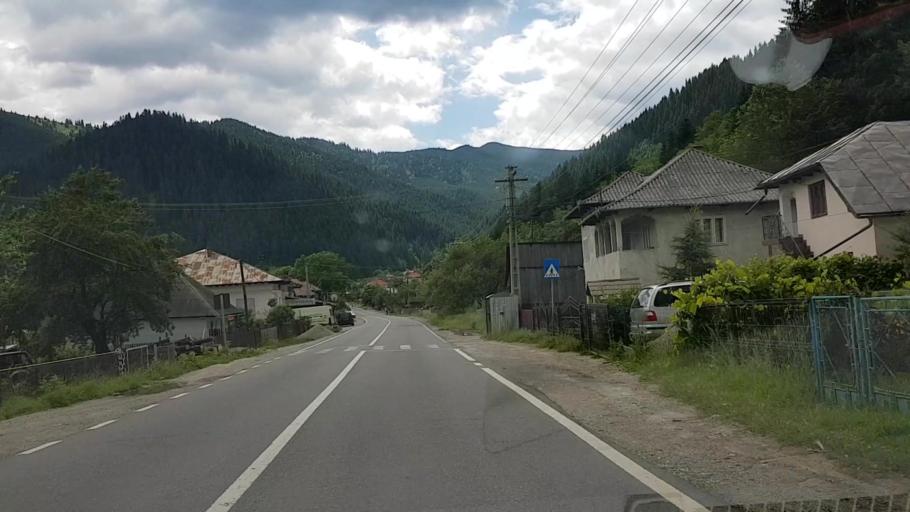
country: RO
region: Neamt
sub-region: Comuna Borca
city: Borca
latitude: 47.2082
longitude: 25.7535
